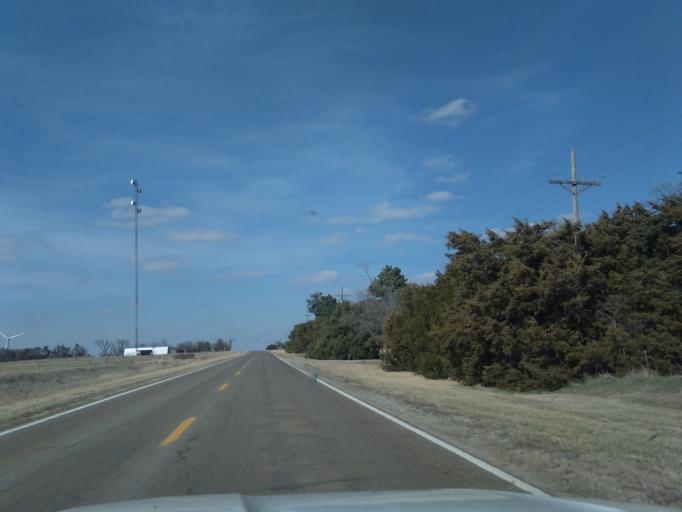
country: US
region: Nebraska
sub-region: Jefferson County
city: Fairbury
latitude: 40.0530
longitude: -96.9351
